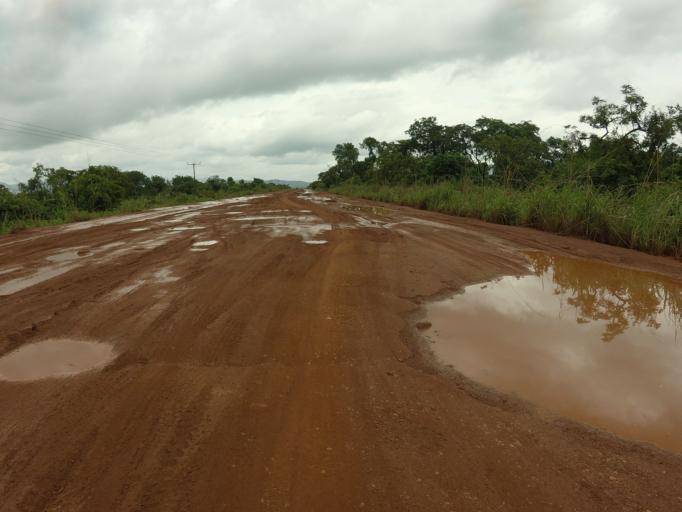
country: GH
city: Kpandae
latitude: 8.3088
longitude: 0.4840
